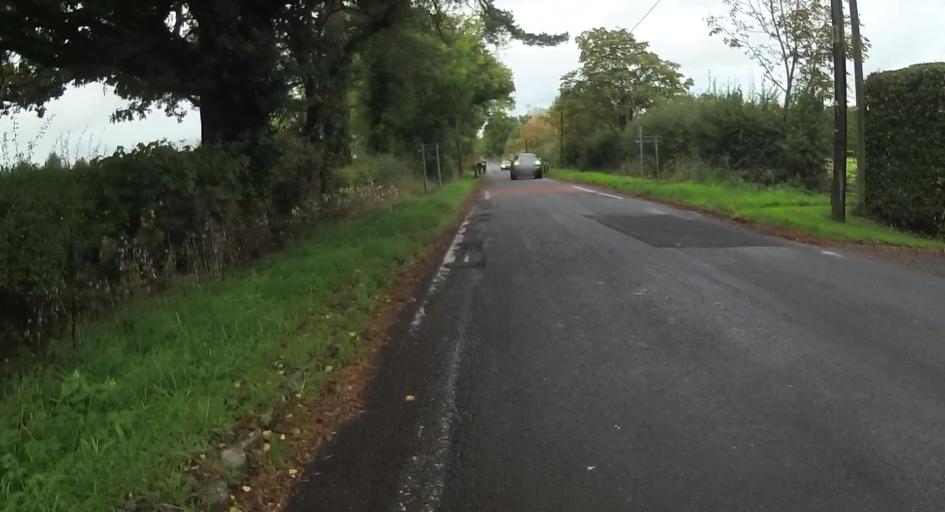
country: GB
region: England
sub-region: Hampshire
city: Tadley
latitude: 51.3145
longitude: -1.1584
